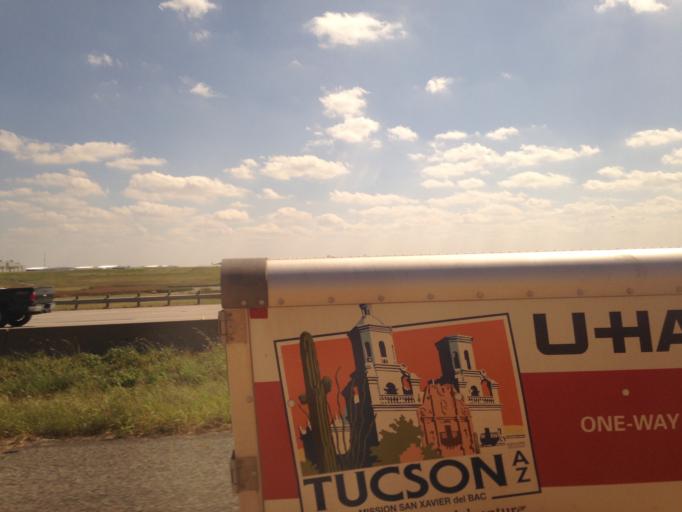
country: US
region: Texas
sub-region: Tarrant County
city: Saginaw
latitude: 32.8347
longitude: -97.3682
